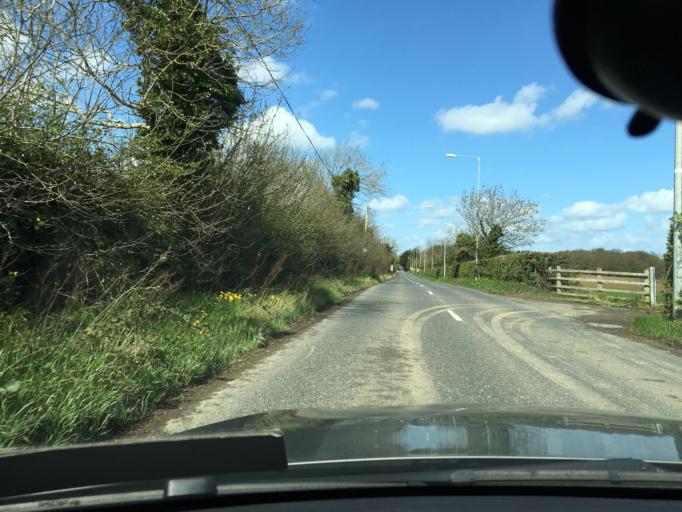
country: IE
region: Leinster
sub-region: Fingal County
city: Blanchardstown
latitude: 53.4250
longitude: -6.3653
